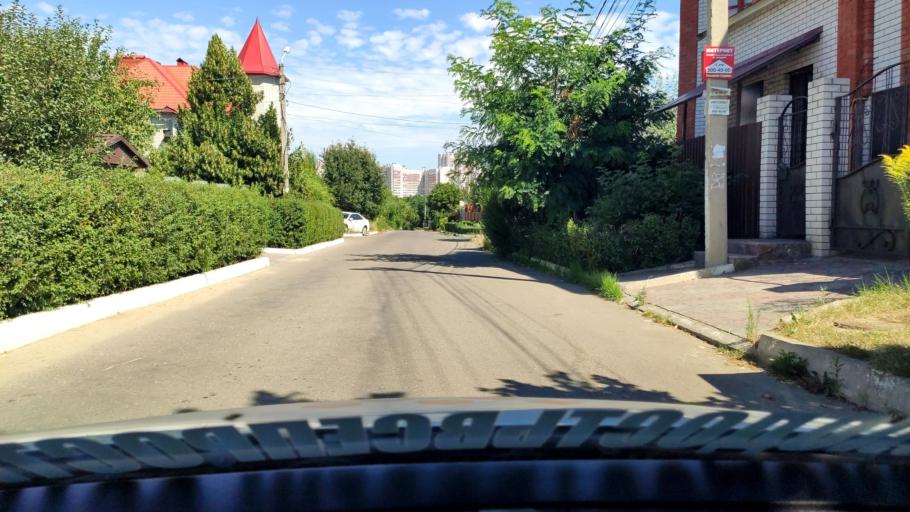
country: RU
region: Voronezj
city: Voronezh
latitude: 51.7051
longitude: 39.1989
